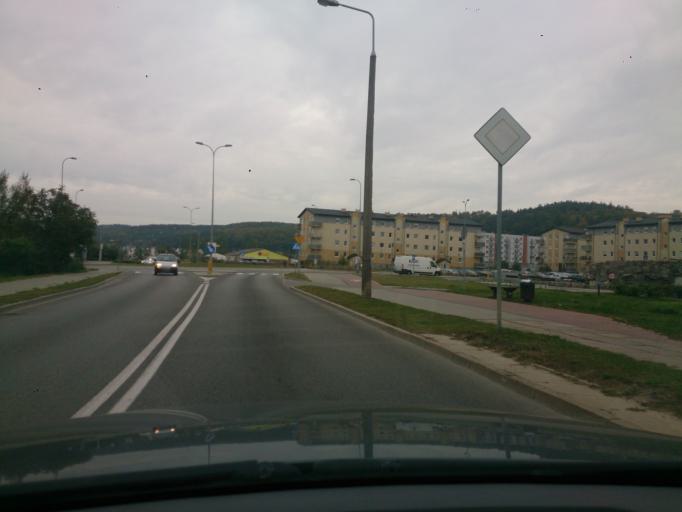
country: PL
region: Pomeranian Voivodeship
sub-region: Powiat wejherowski
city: Reda
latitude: 54.5952
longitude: 18.3616
